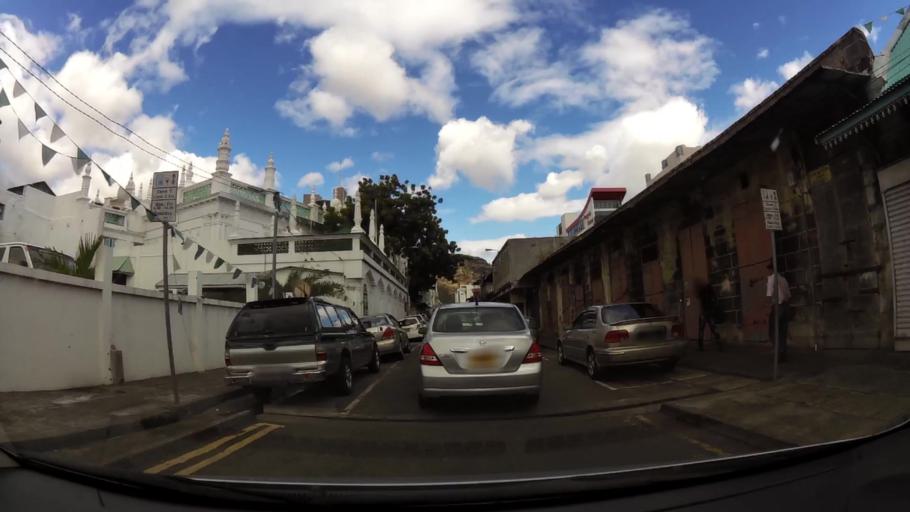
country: MU
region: Port Louis
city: Port Louis
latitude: -20.1593
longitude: 57.5051
